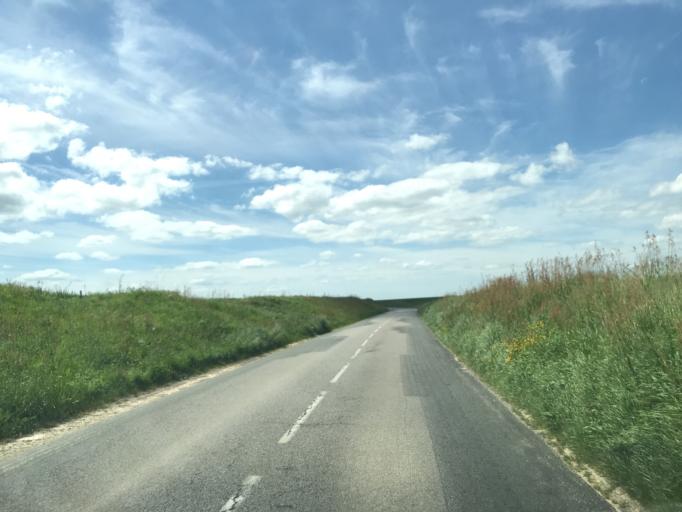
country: FR
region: Haute-Normandie
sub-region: Departement de l'Eure
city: Le Neubourg
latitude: 49.1482
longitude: 0.8857
